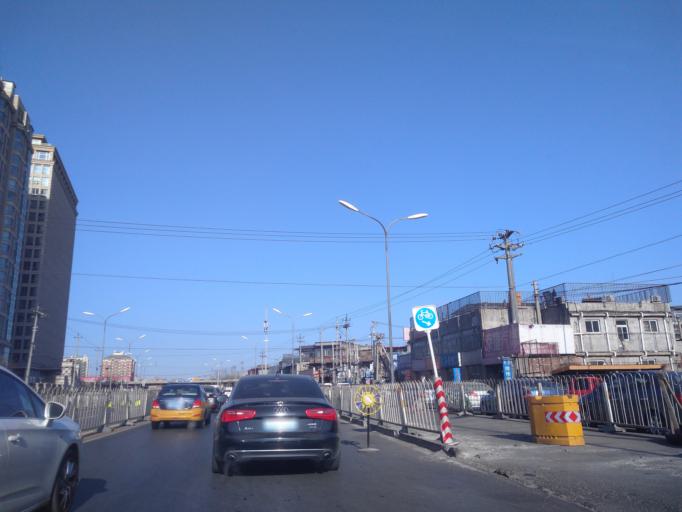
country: CN
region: Beijing
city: Jiugong
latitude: 39.8345
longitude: 116.4689
